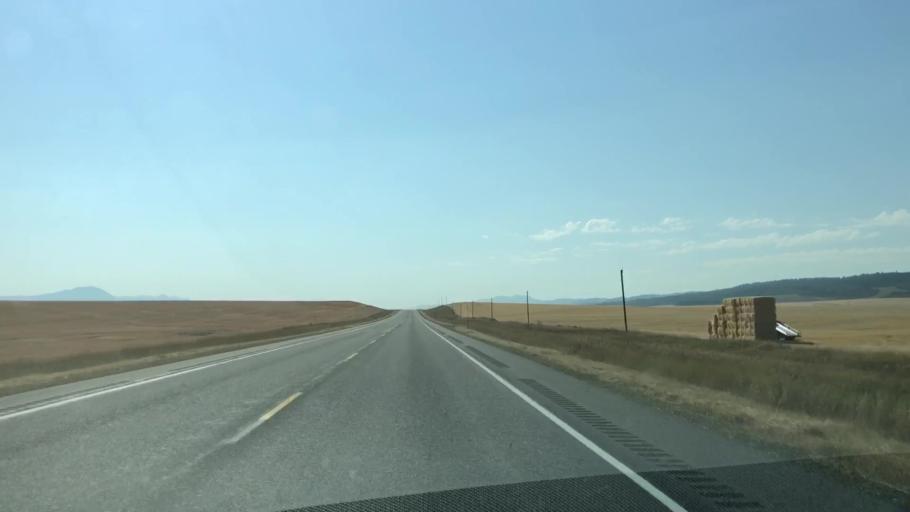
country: US
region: Idaho
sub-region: Madison County
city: Rexburg
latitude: 43.5473
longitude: -111.5261
